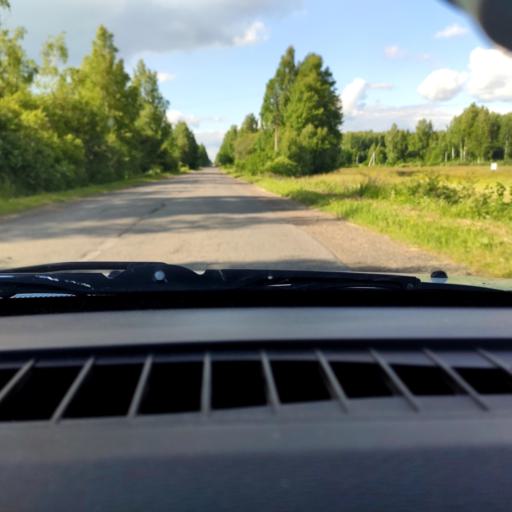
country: RU
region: Perm
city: Uinskoye
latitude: 57.2396
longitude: 56.5318
